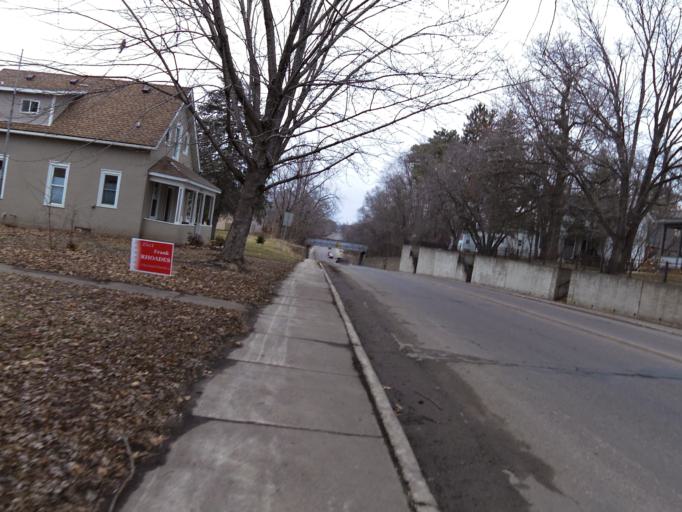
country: US
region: Wisconsin
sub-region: Saint Croix County
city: North Hudson
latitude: 44.9852
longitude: -92.7574
